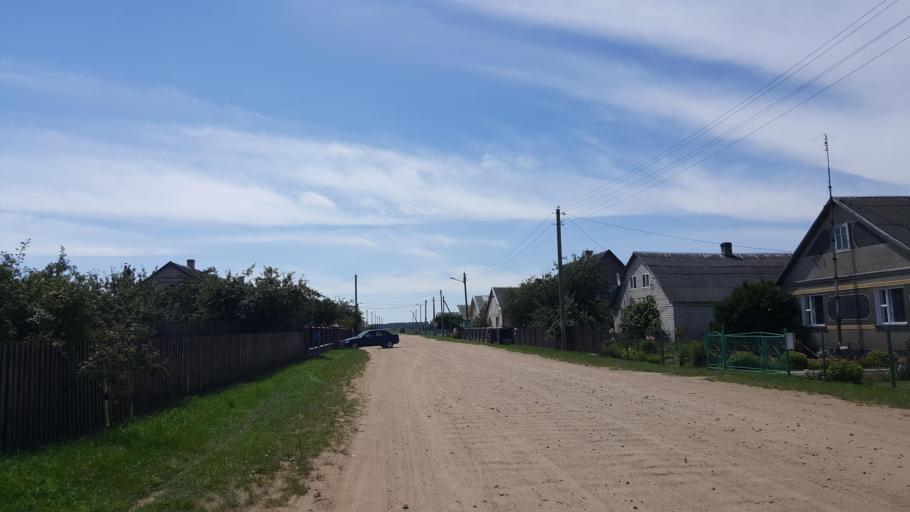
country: BY
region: Brest
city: Pruzhany
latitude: 52.5534
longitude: 24.2057
